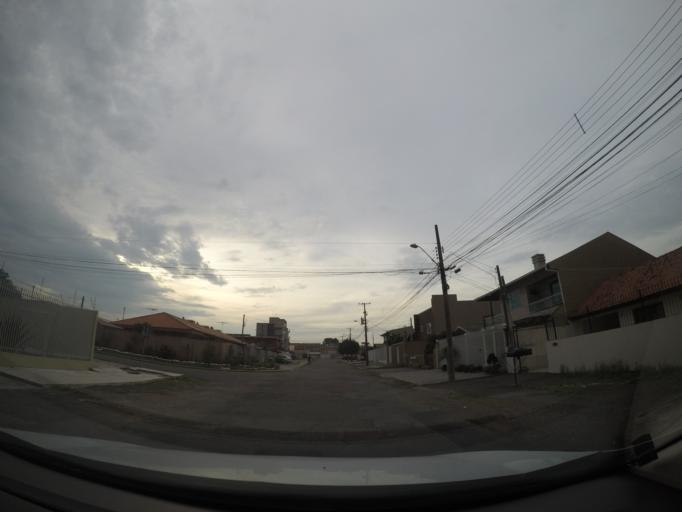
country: BR
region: Parana
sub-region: Sao Jose Dos Pinhais
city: Sao Jose dos Pinhais
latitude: -25.5222
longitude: -49.2328
